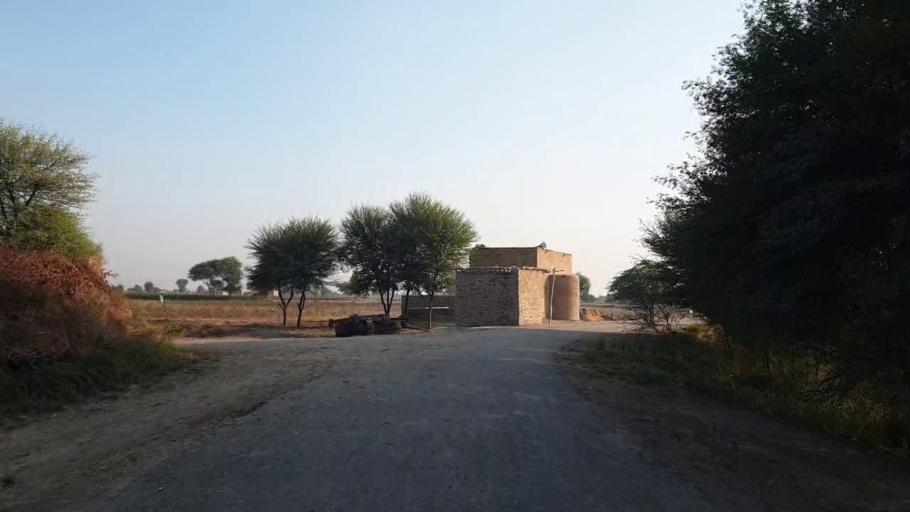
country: PK
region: Sindh
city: Sehwan
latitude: 26.4505
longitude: 67.7838
